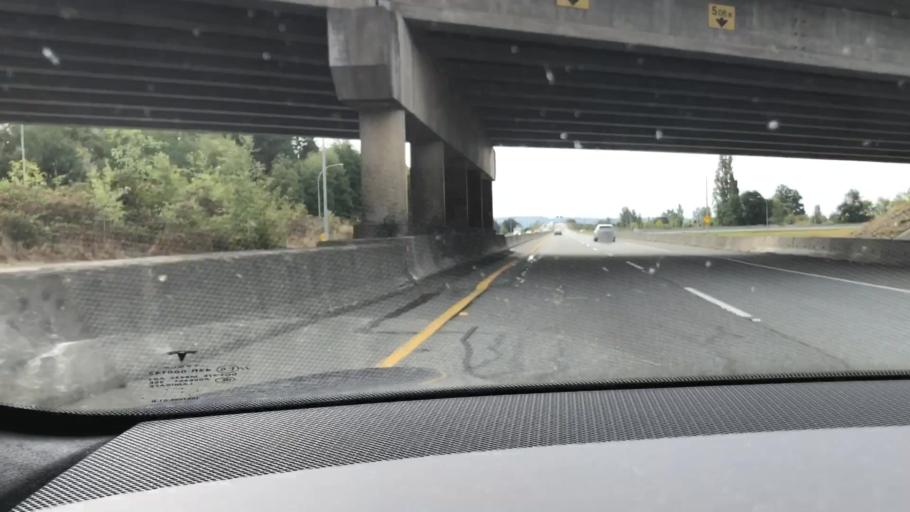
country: CA
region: British Columbia
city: Delta
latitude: 49.1026
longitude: -122.9006
